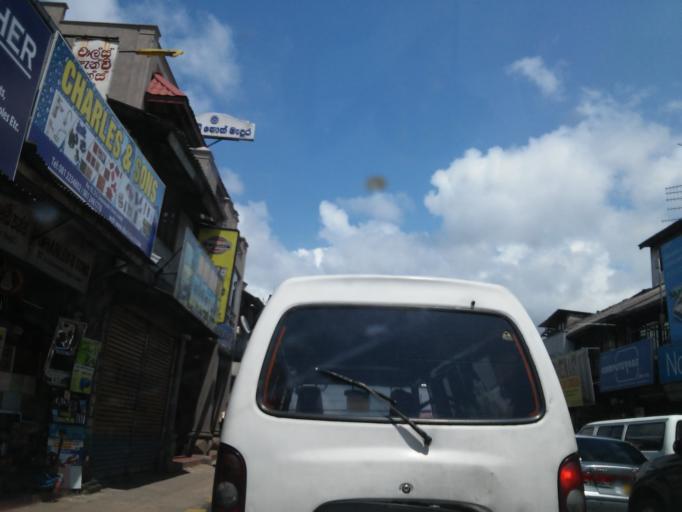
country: LK
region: Central
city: Kandy
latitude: 7.2957
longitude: 80.6379
